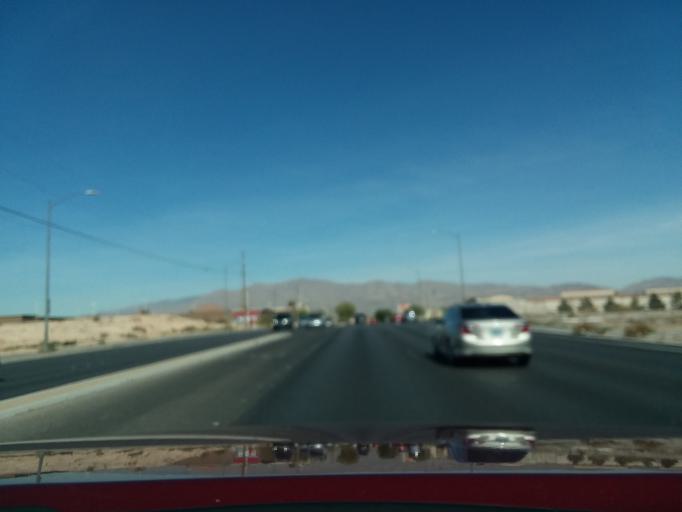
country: US
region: Nevada
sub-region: Clark County
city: North Las Vegas
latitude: 36.2354
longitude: -115.1619
